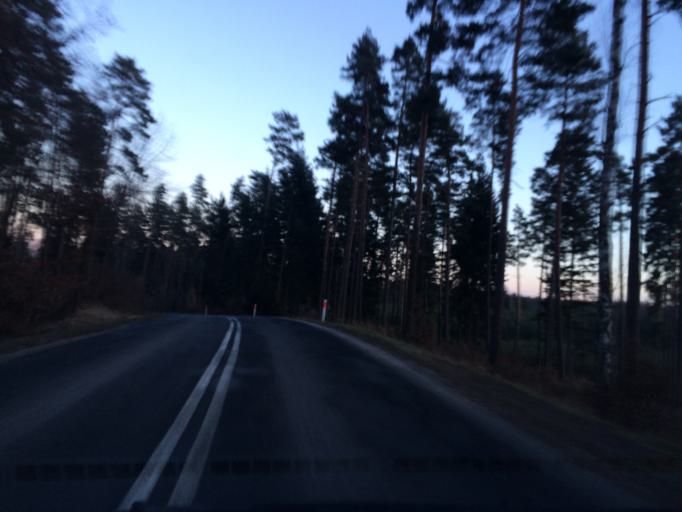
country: PL
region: Lower Silesian Voivodeship
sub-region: Powiat zlotoryjski
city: Olszanica
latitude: 51.1230
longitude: 15.7269
